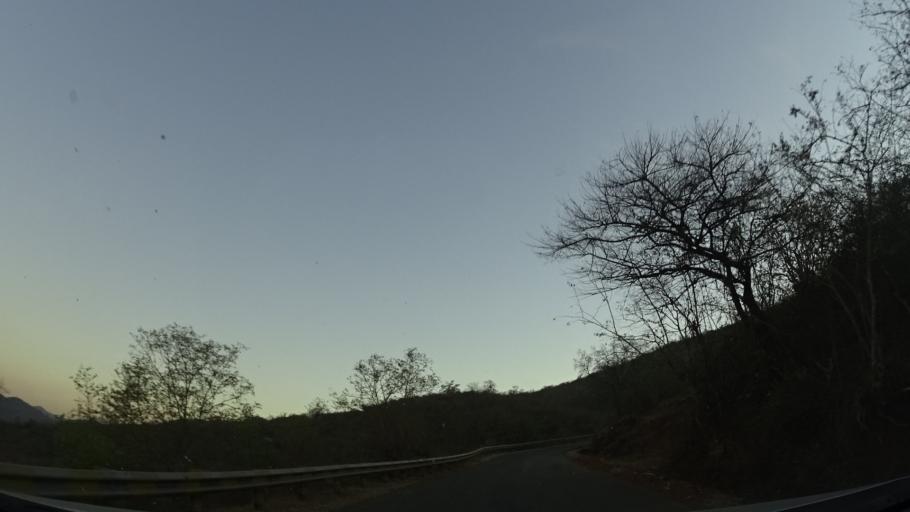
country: IN
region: Karnataka
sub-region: Chikmagalur
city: Birur
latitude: 13.5515
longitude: 75.8235
